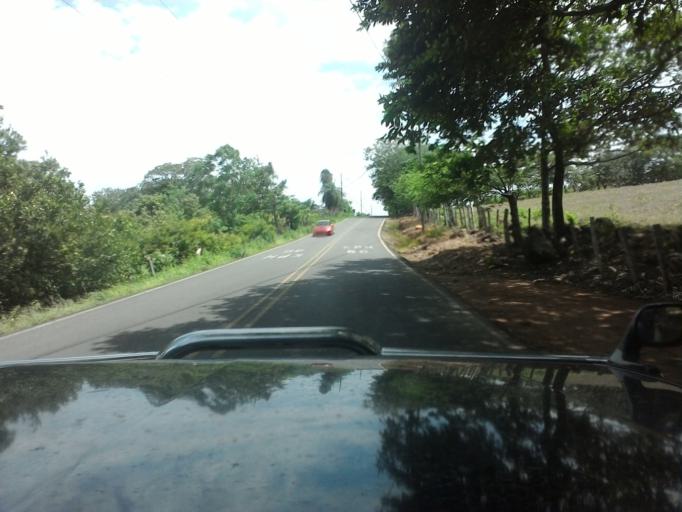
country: CR
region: Puntarenas
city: Miramar
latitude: 10.1193
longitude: -84.8278
